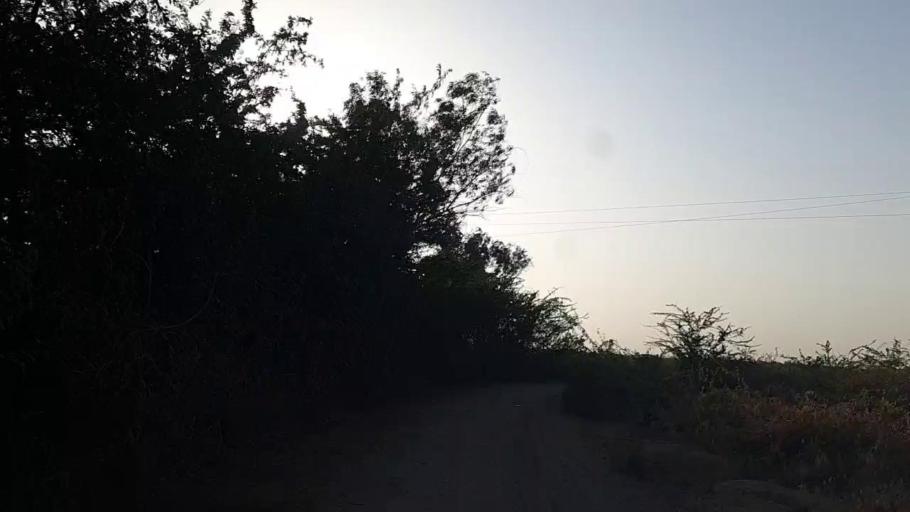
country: PK
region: Sindh
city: Naukot
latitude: 24.6432
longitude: 69.2525
